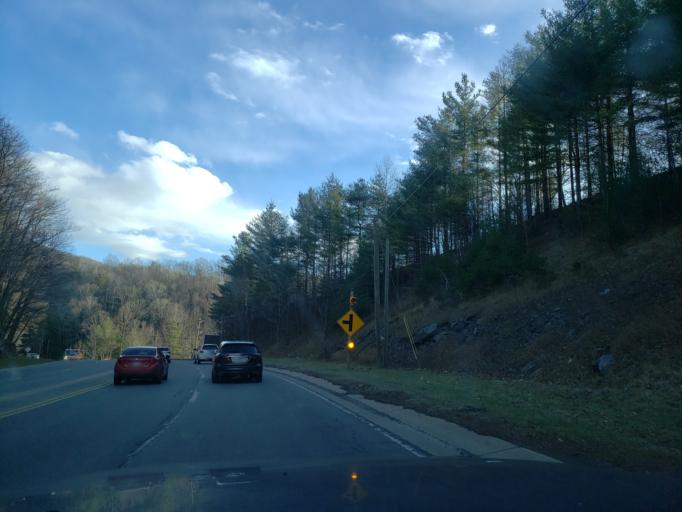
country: US
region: North Carolina
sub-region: Watauga County
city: Boone
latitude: 36.1827
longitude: -81.6505
